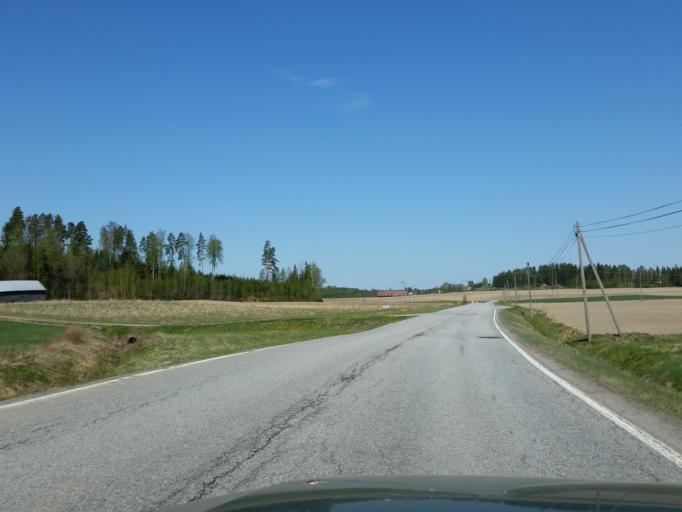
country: FI
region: Uusimaa
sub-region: Helsinki
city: Lohja
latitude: 60.1782
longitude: 24.0488
